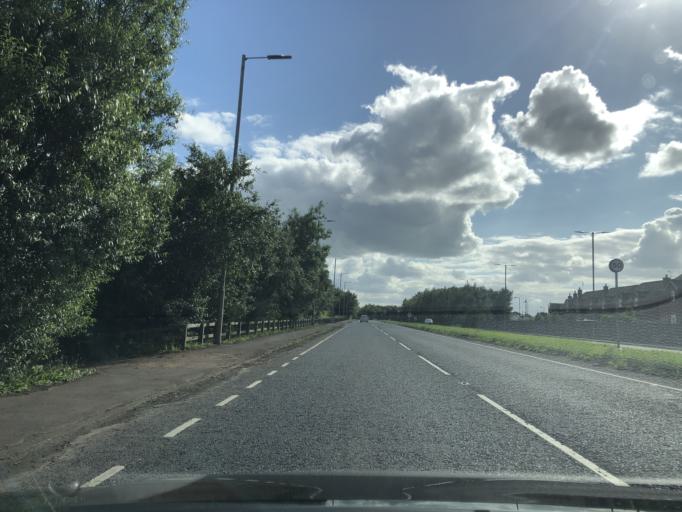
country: GB
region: Northern Ireland
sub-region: Ards District
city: Comber
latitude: 54.5535
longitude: -5.7251
